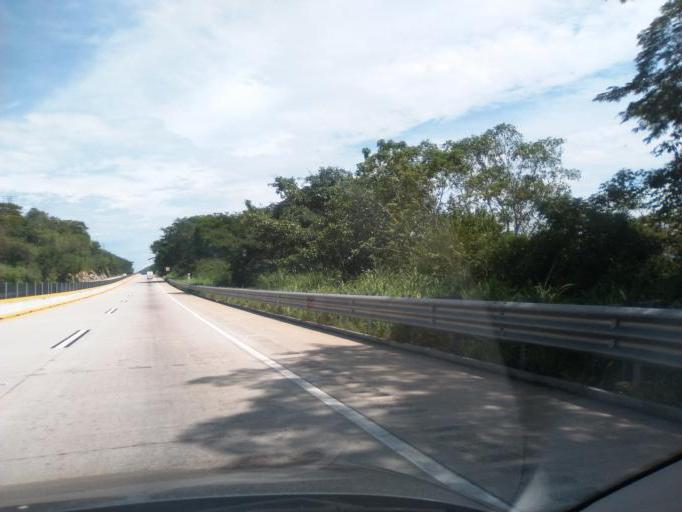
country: MX
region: Guerrero
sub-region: Acapulco de Juarez
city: Kilometro 30
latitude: 17.0025
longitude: -99.6779
